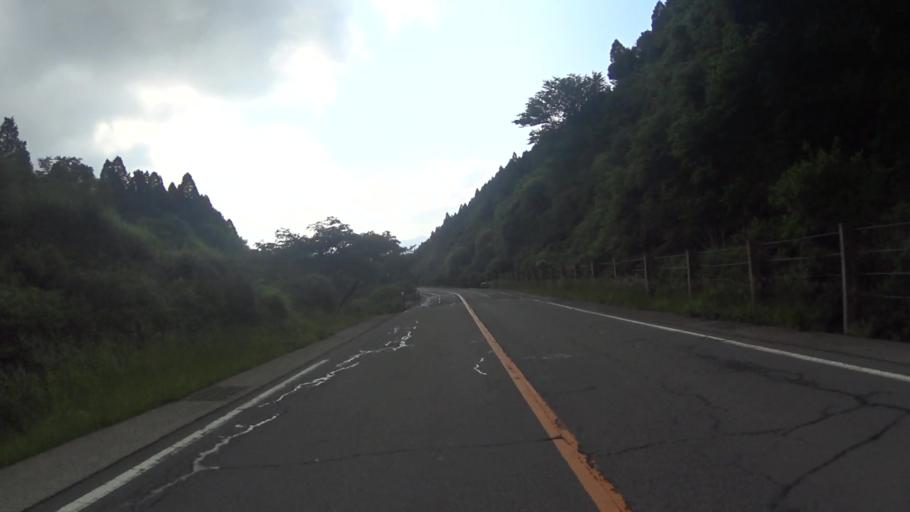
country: JP
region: Kumamoto
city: Aso
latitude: 32.8885
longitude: 131.0538
